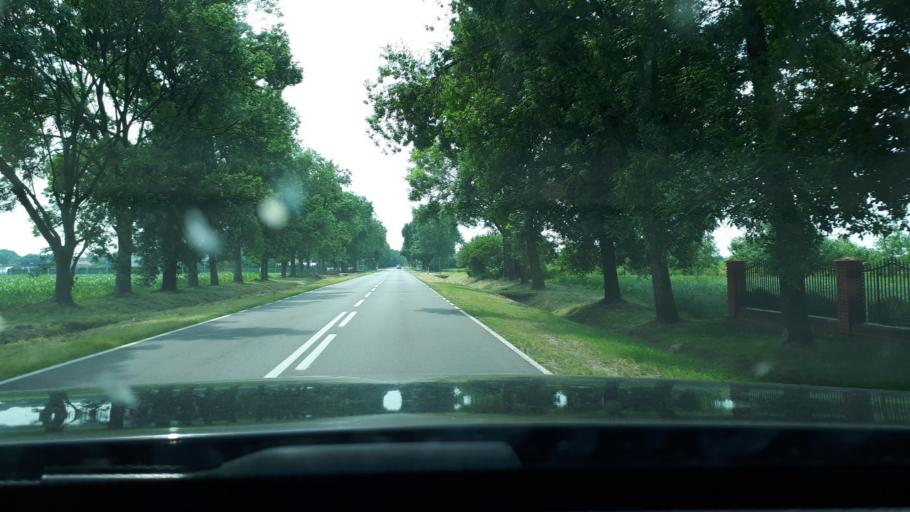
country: PL
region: Masovian Voivodeship
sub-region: Powiat sochaczewski
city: Paprotnia
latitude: 52.2639
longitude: 20.3656
